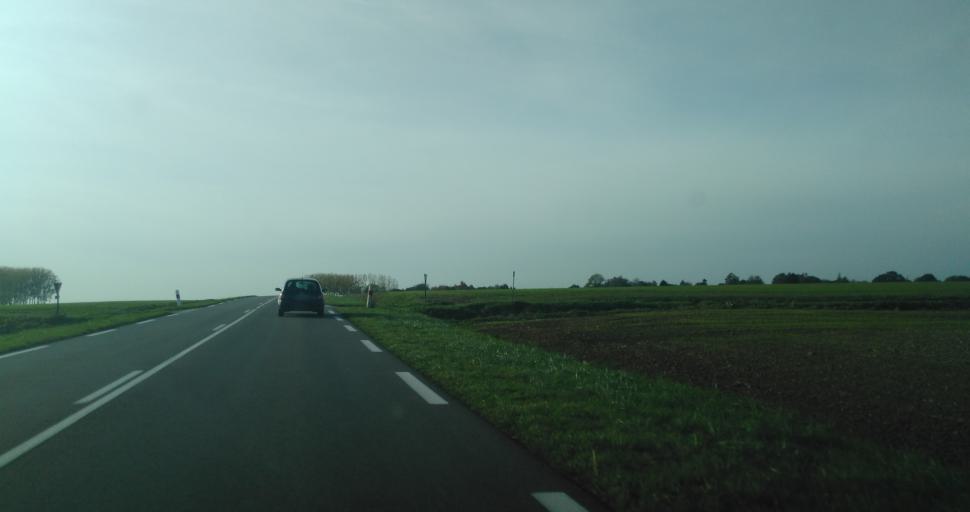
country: FR
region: Haute-Normandie
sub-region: Departement de l'Eure
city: Hauville
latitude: 49.3577
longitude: 0.7740
